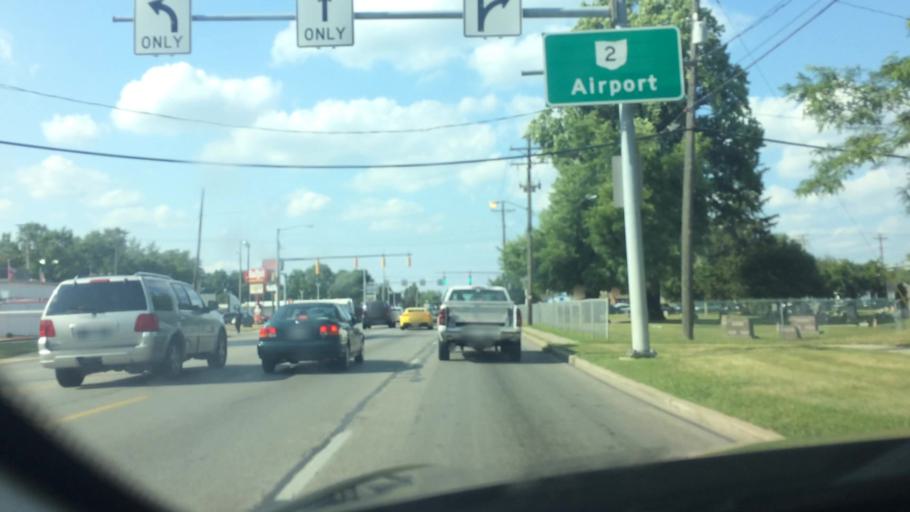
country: US
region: Ohio
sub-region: Lucas County
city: Ottawa Hills
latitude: 41.6232
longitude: -83.6258
